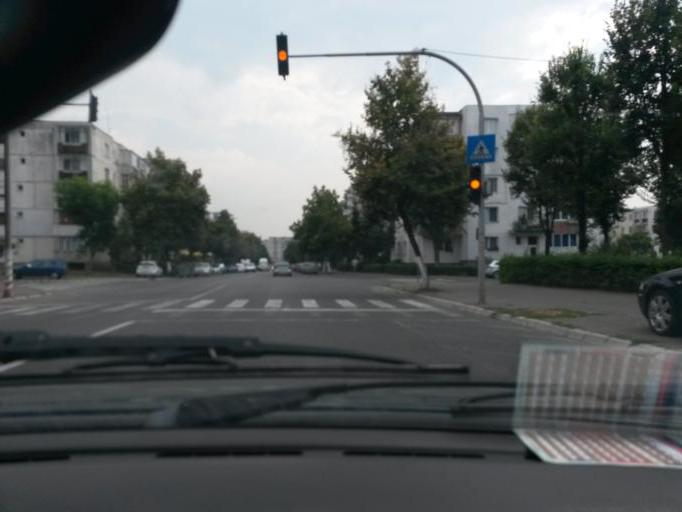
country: RO
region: Mures
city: Targu-Mures
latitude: 46.5390
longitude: 24.5868
